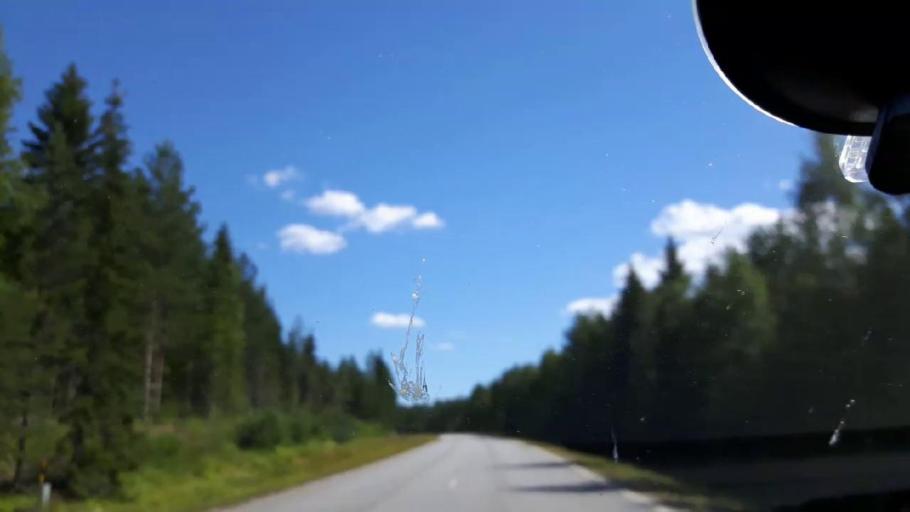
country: SE
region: Vaesternorrland
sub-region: Ange Kommun
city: Fransta
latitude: 62.7107
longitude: 16.3442
